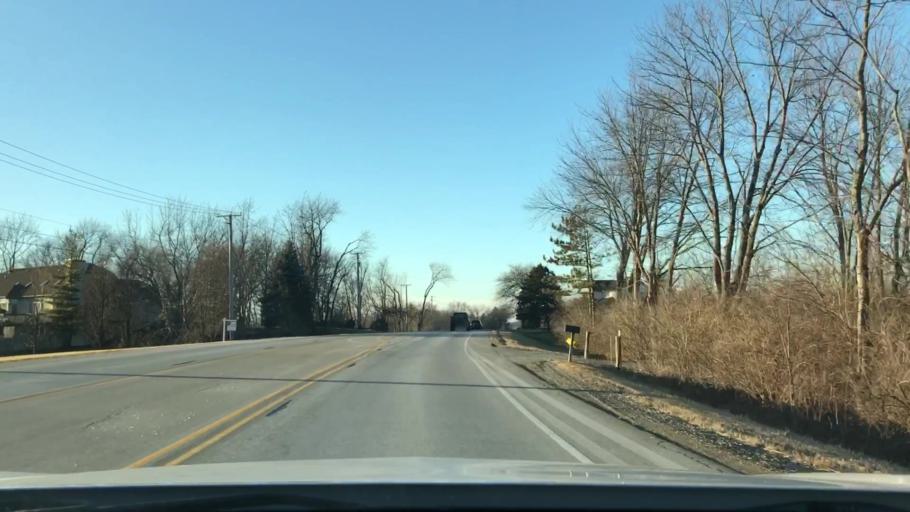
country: US
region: Illinois
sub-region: Kane County
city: Gilberts
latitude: 42.0792
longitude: -88.3798
